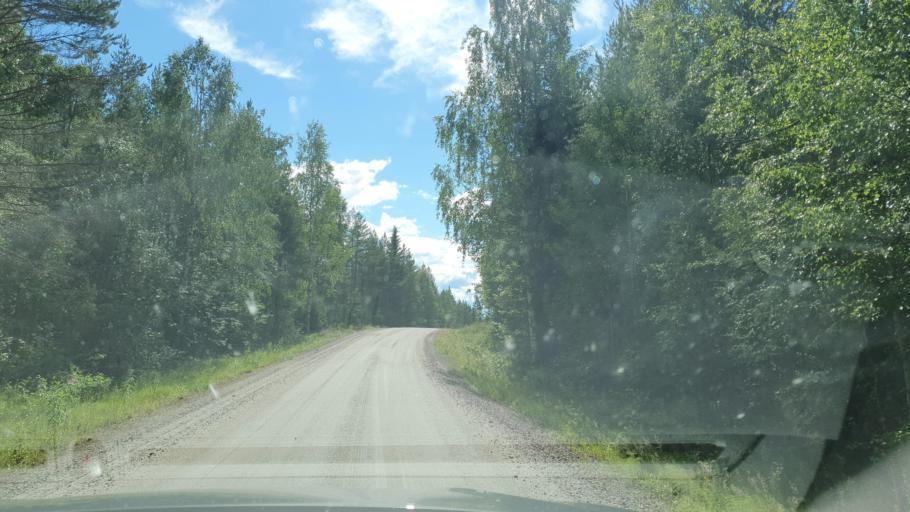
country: FI
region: Kainuu
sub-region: Kehys-Kainuu
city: Kuhmo
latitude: 64.1642
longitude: 29.8567
